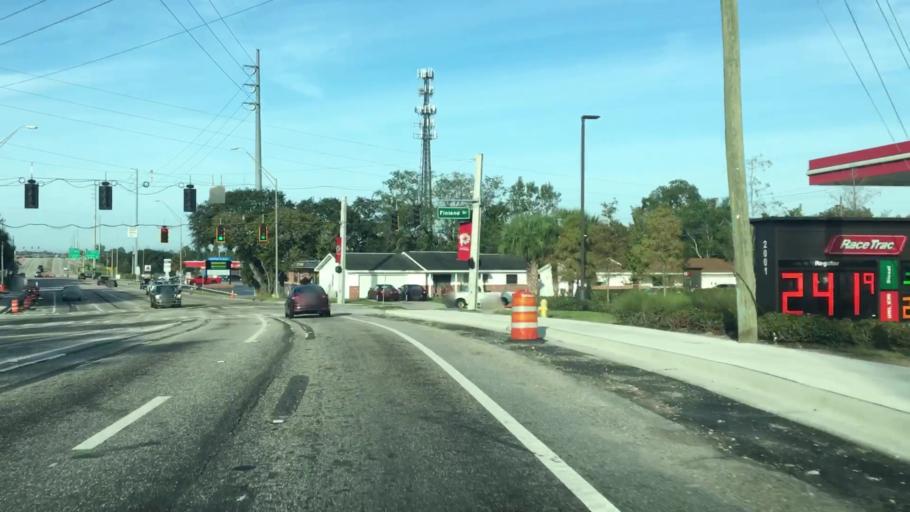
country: US
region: Florida
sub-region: Volusia County
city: Deltona
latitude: 28.9113
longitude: -81.2646
